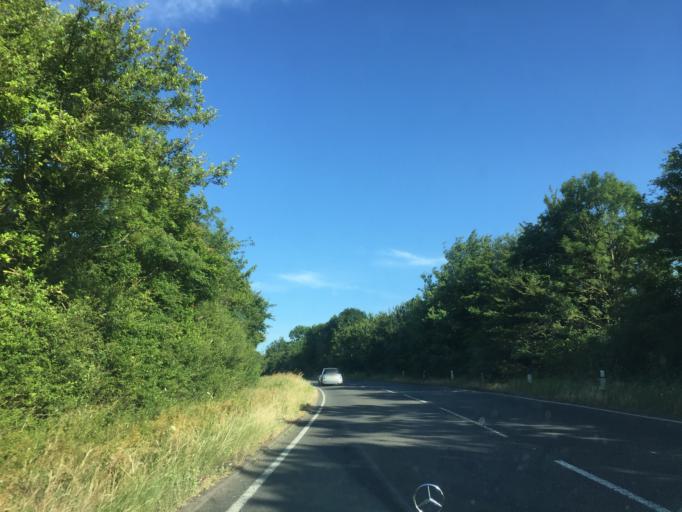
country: GB
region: England
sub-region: Oxfordshire
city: Wheatley
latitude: 51.7349
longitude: -1.0809
